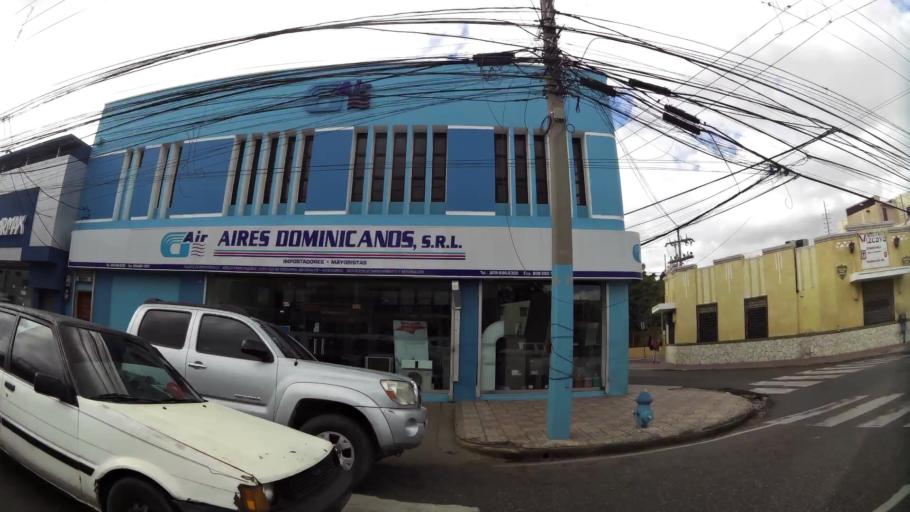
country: DO
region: Nacional
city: San Carlos
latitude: 18.4798
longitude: -69.9006
